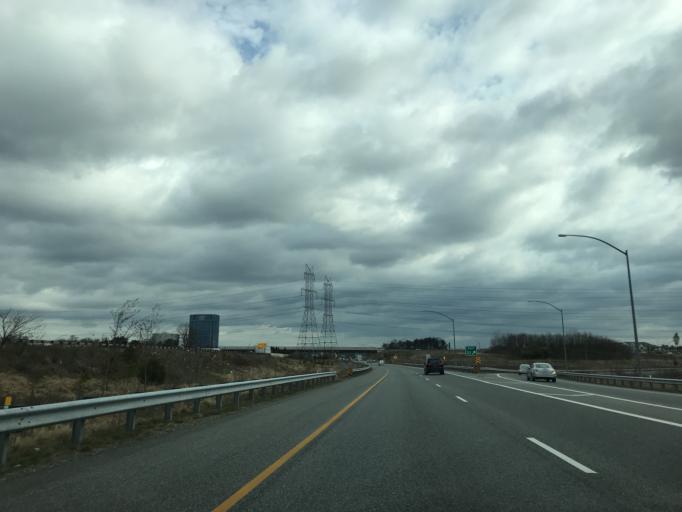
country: US
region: Maryland
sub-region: Prince George's County
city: West Laurel
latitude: 39.0809
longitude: -76.8991
